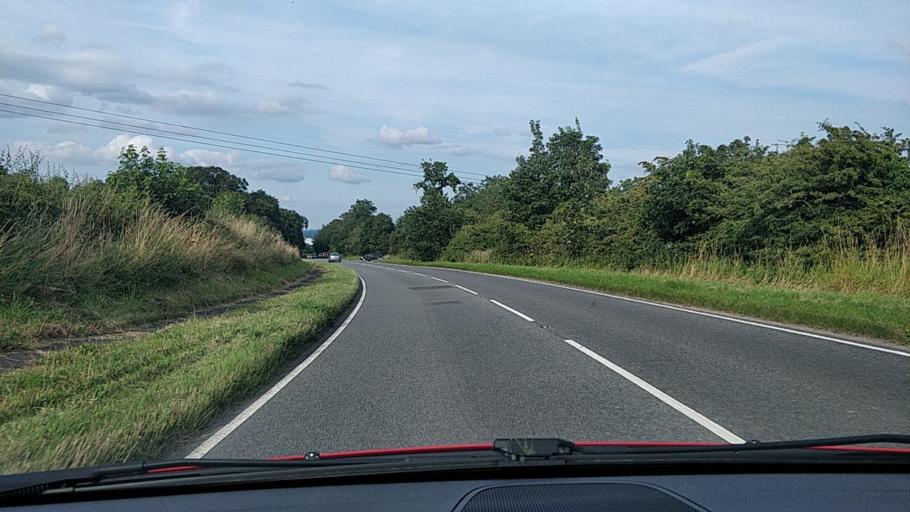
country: GB
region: Wales
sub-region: County of Flintshire
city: Penyffordd
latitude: 53.1552
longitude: -3.0237
